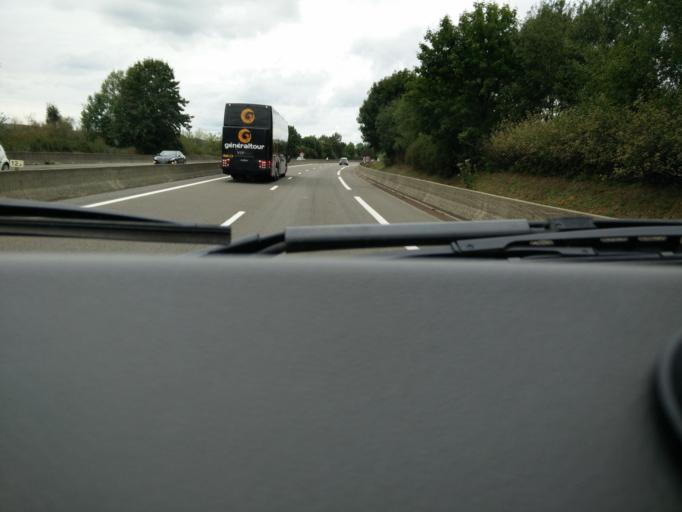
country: FR
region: Champagne-Ardenne
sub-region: Departement des Ardennes
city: Balan
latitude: 49.6827
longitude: 4.9628
